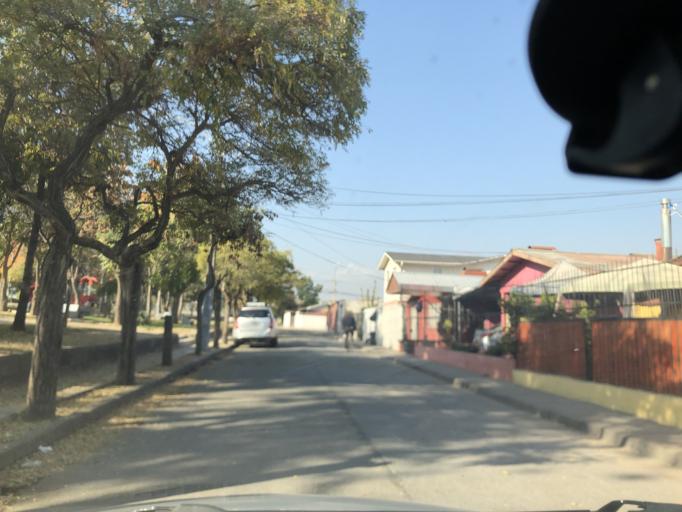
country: CL
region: Santiago Metropolitan
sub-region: Provincia de Cordillera
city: Puente Alto
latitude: -33.6134
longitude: -70.5601
